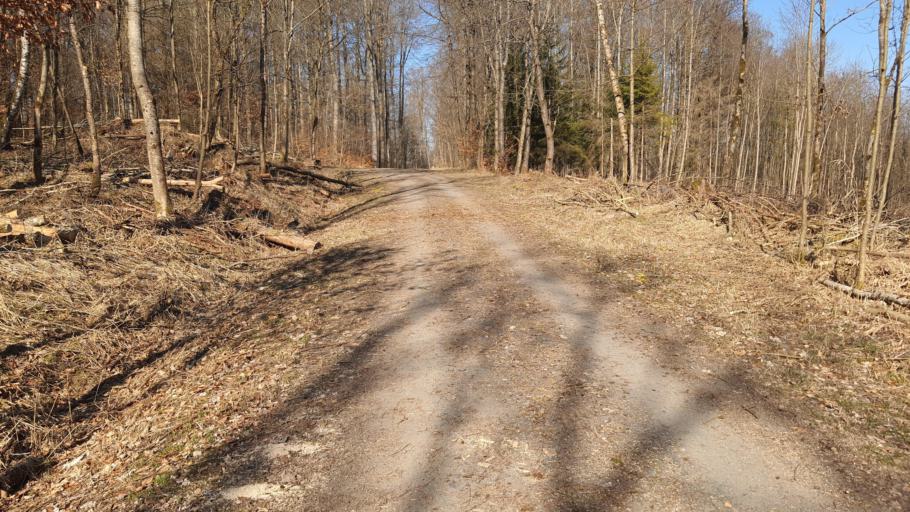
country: DE
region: Hesse
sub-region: Regierungsbezirk Giessen
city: Greifenstein
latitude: 50.6284
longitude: 8.2713
